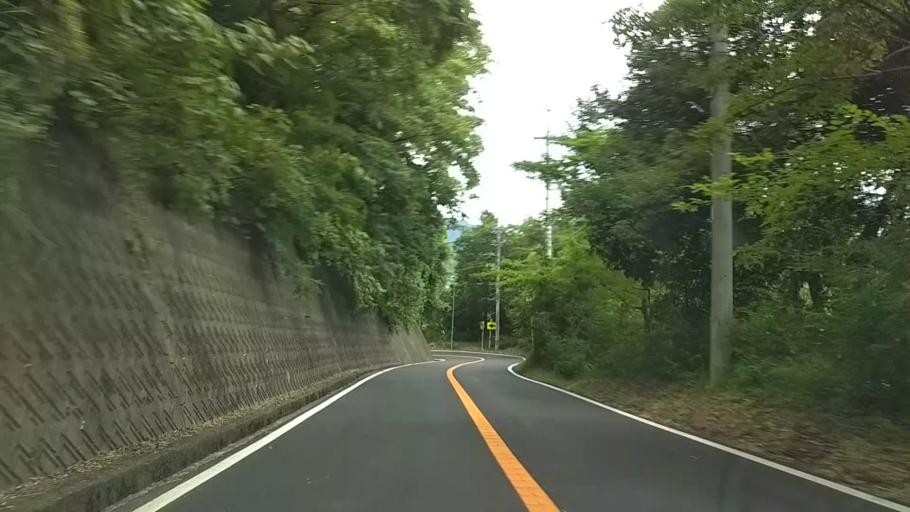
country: JP
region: Yamanashi
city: Uenohara
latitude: 35.6064
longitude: 139.1236
